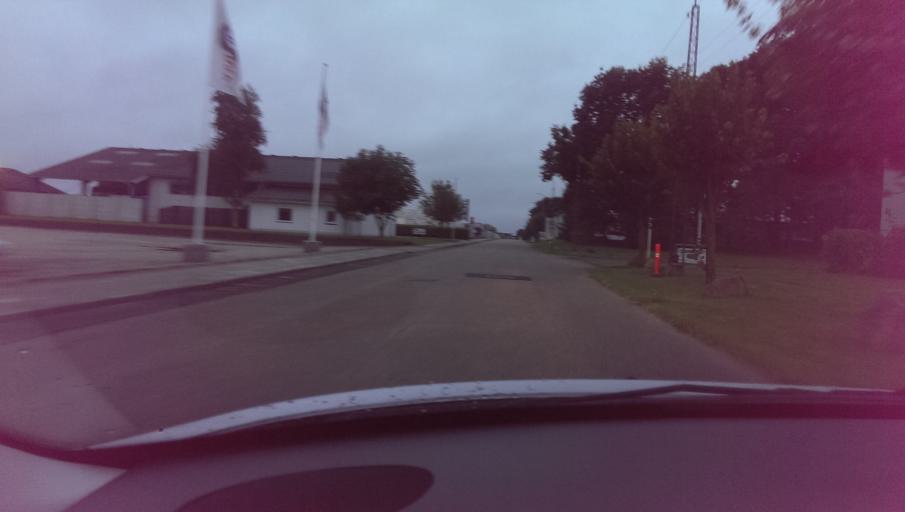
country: DK
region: South Denmark
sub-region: Varde Kommune
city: Olgod
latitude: 55.8134
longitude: 8.6255
